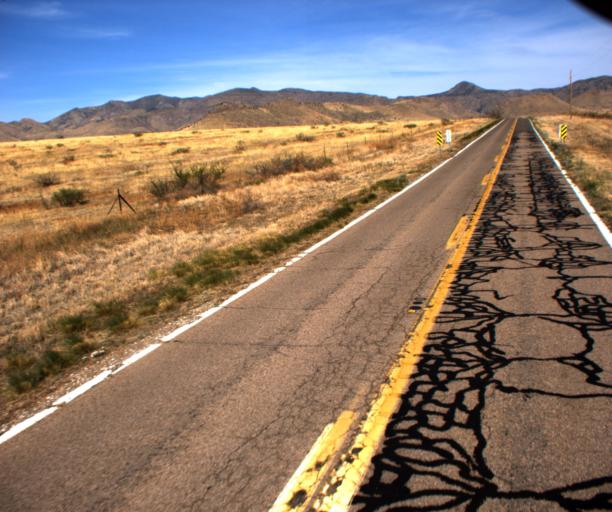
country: US
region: Arizona
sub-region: Cochise County
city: Willcox
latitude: 32.0068
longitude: -109.4302
